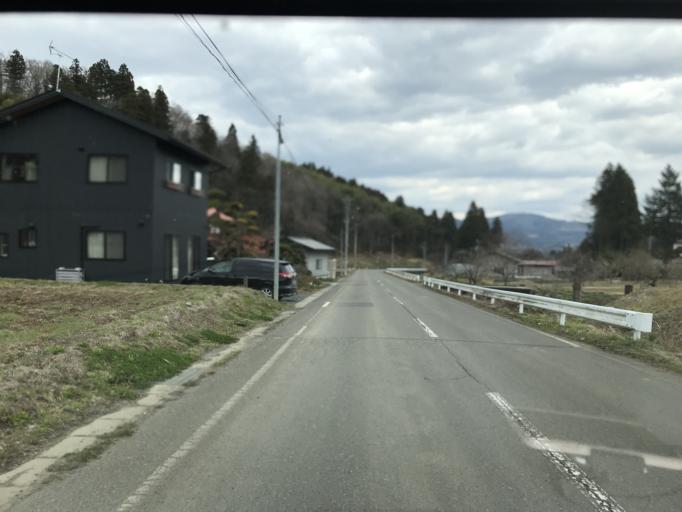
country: JP
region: Iwate
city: Ichinoseki
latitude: 38.9714
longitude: 141.1023
